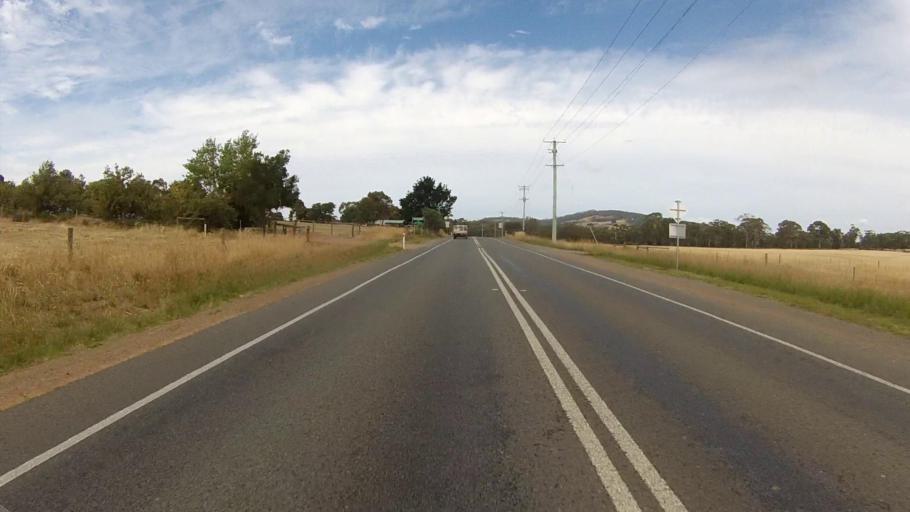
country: AU
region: Tasmania
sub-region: Clarence
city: Sandford
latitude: -42.9325
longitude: 147.4915
